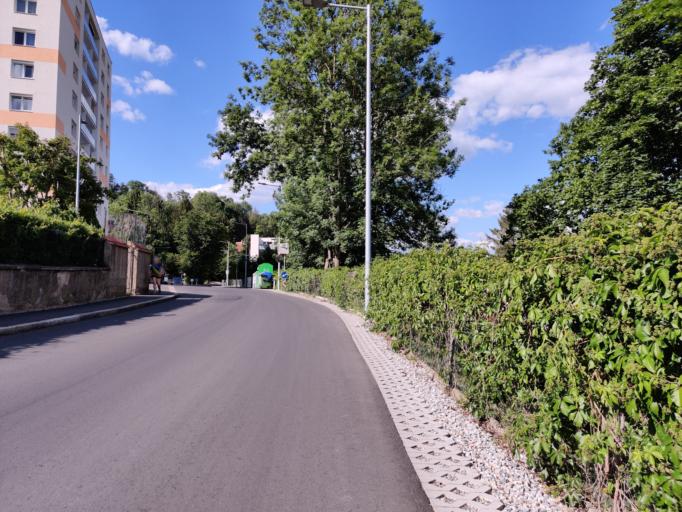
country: AT
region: Styria
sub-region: Graz Stadt
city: Wetzelsdorf
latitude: 47.0473
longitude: 15.3874
